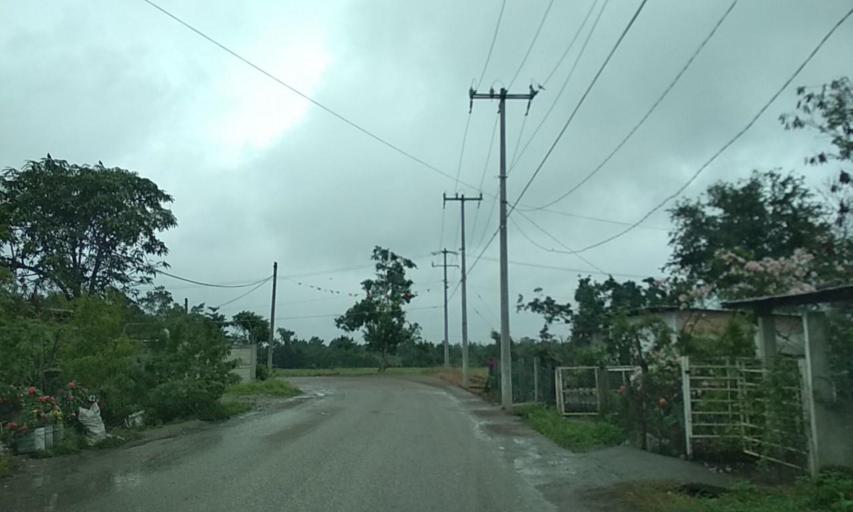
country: MX
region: Veracruz
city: Agua Dulce
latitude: 20.3584
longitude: -97.3366
